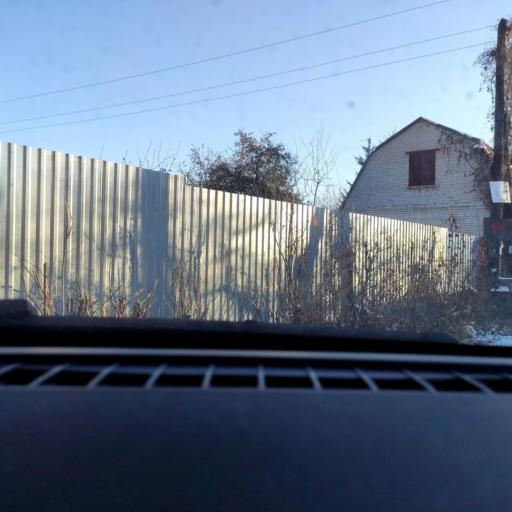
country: RU
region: Voronezj
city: Maslovka
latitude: 51.6067
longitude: 39.2715
